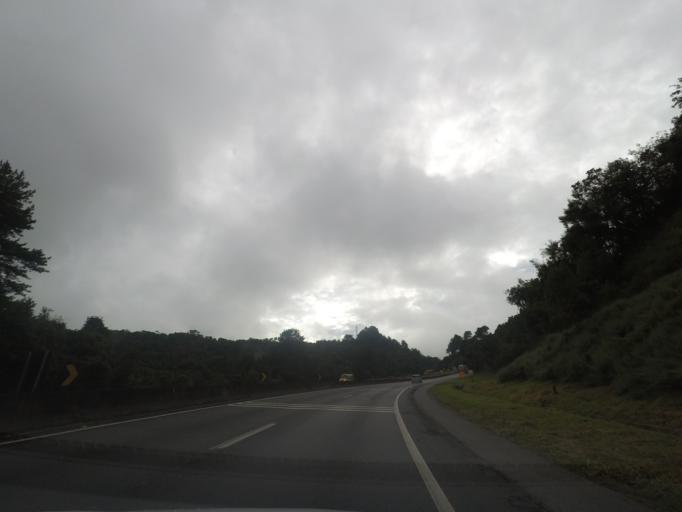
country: BR
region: Parana
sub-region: Campina Grande Do Sul
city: Campina Grande do Sul
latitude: -25.1929
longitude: -48.8879
